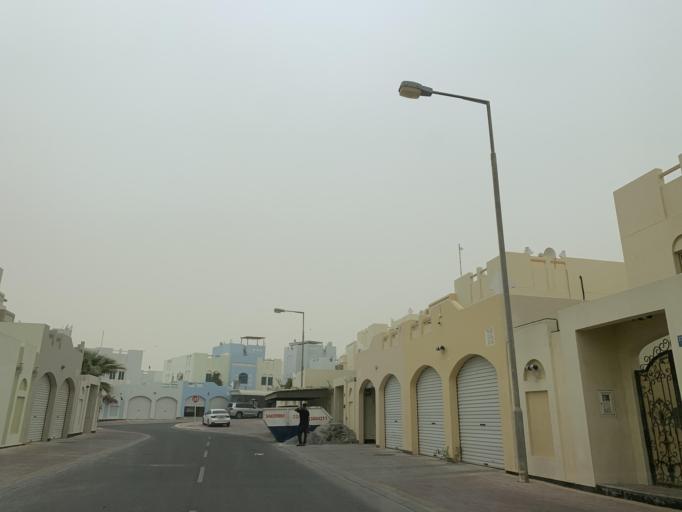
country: BH
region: Central Governorate
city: Madinat Hamad
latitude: 26.1374
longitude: 50.5133
